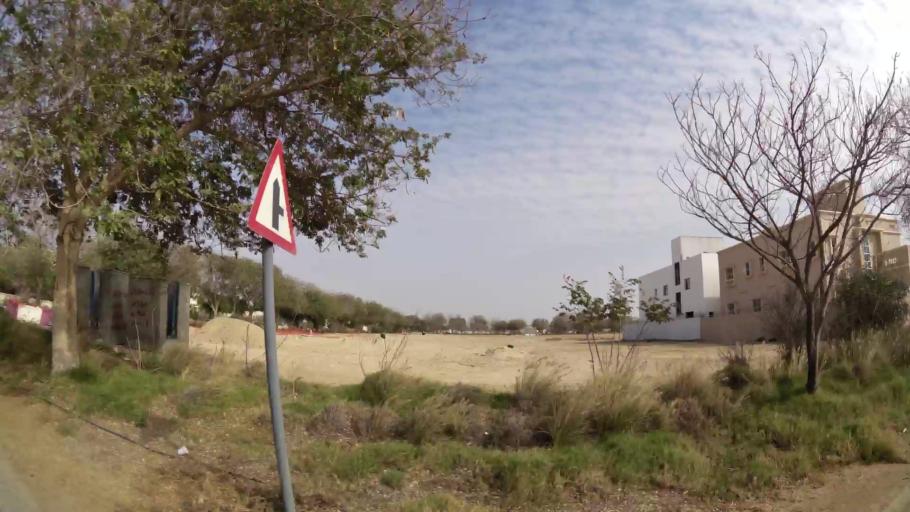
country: AE
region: Abu Dhabi
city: Abu Dhabi
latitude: 24.6077
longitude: 54.7000
